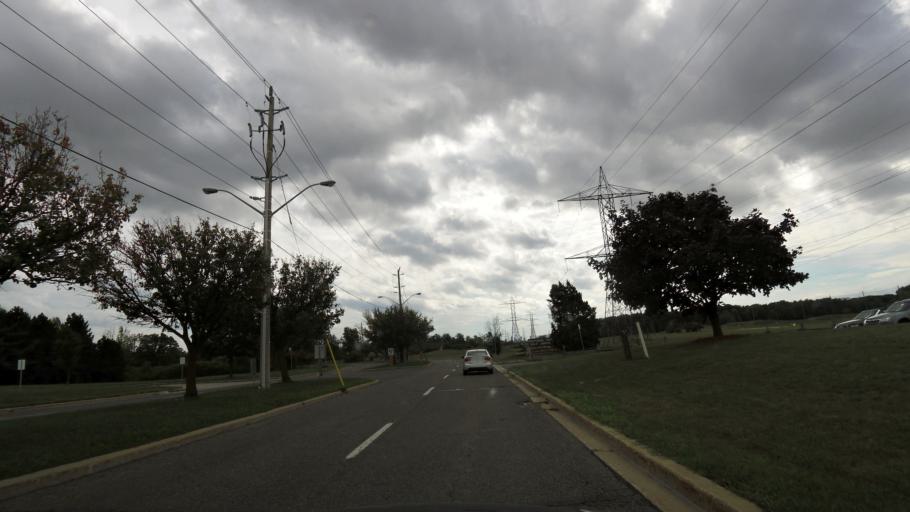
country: CA
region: Ontario
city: Etobicoke
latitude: 43.6492
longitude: -79.5964
